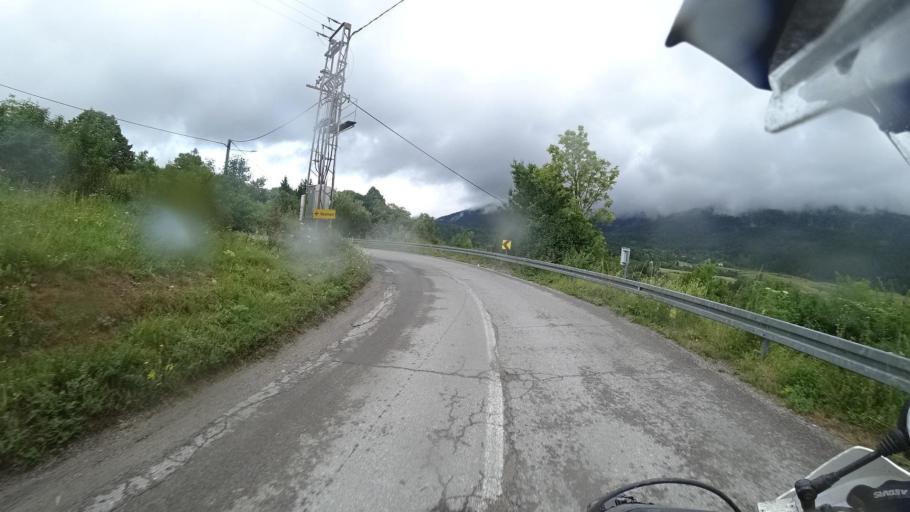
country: HR
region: Karlovacka
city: Plaski
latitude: 45.0161
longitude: 15.4168
